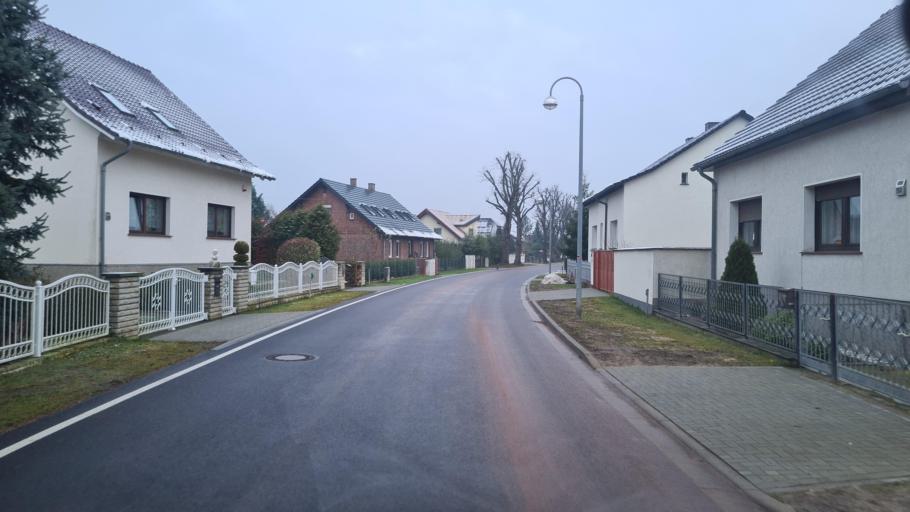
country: DE
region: Brandenburg
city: Storkow
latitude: 52.2888
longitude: 13.8811
